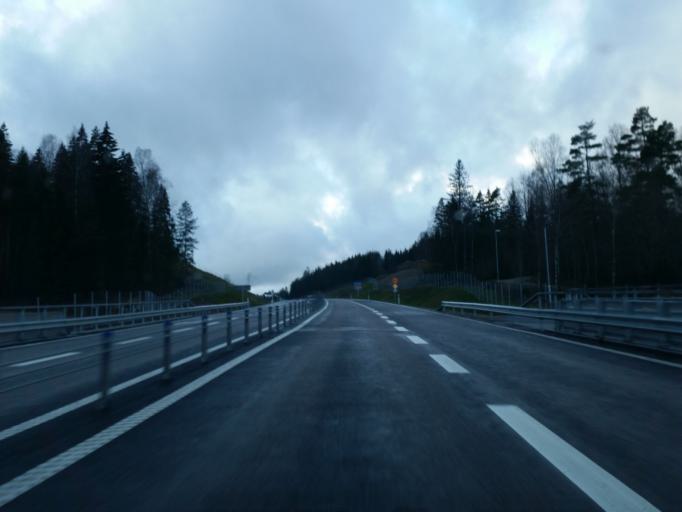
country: SE
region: Vaestra Goetaland
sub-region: Boras Kommun
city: Boras
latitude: 57.6990
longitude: 12.9060
